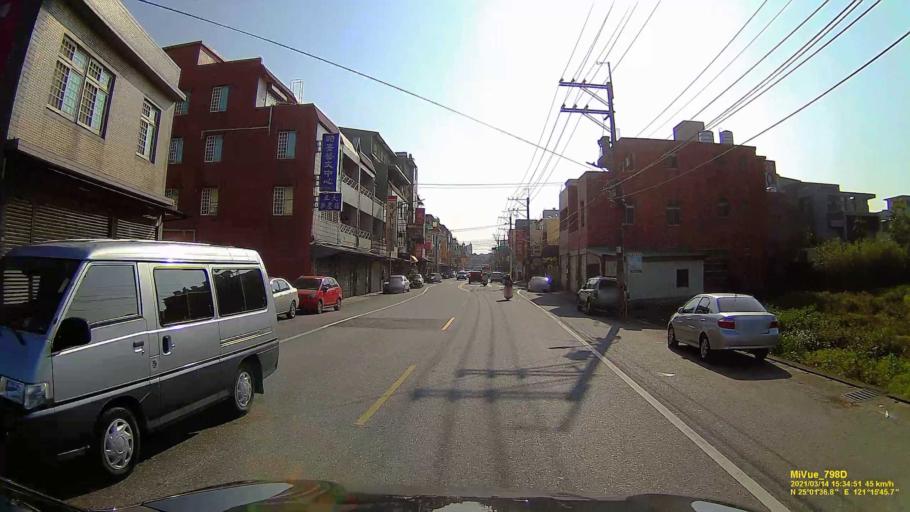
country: TW
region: Taiwan
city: Taoyuan City
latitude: 25.0267
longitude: 121.2625
